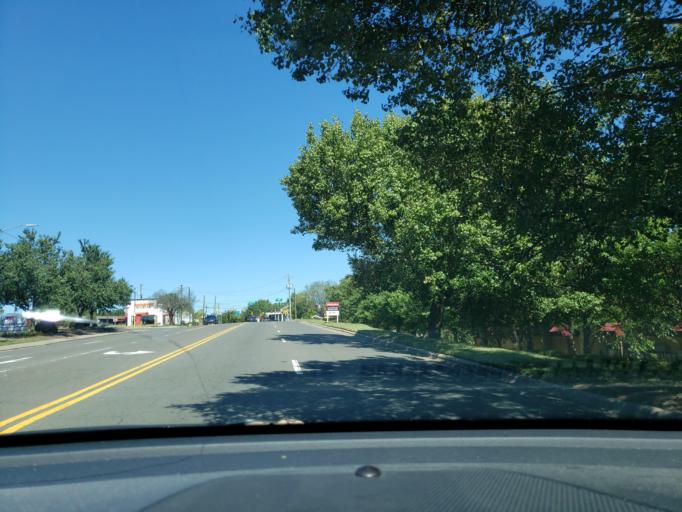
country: US
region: North Carolina
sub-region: Durham County
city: Durham
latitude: 35.9663
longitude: -78.9610
